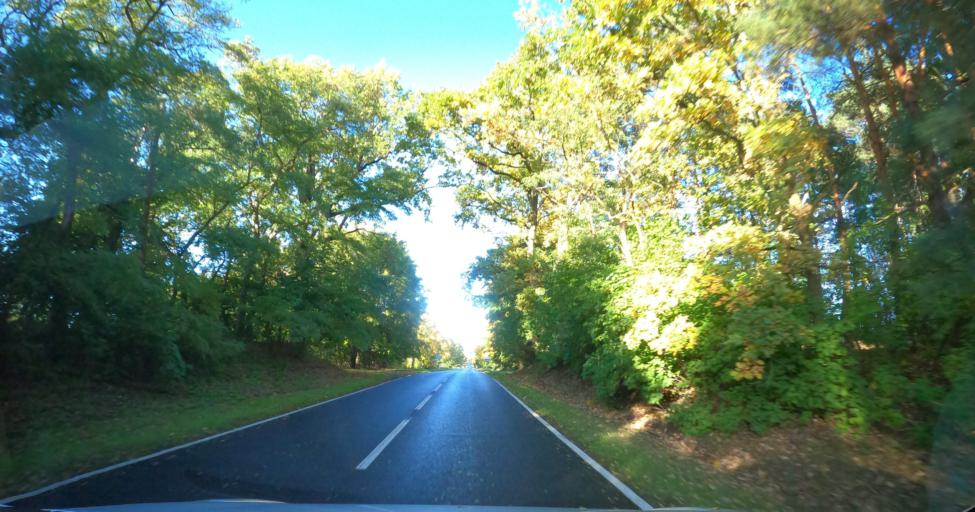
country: PL
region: Lubusz
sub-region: Powiat zielonogorski
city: Zabor
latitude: 51.9381
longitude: 15.6640
